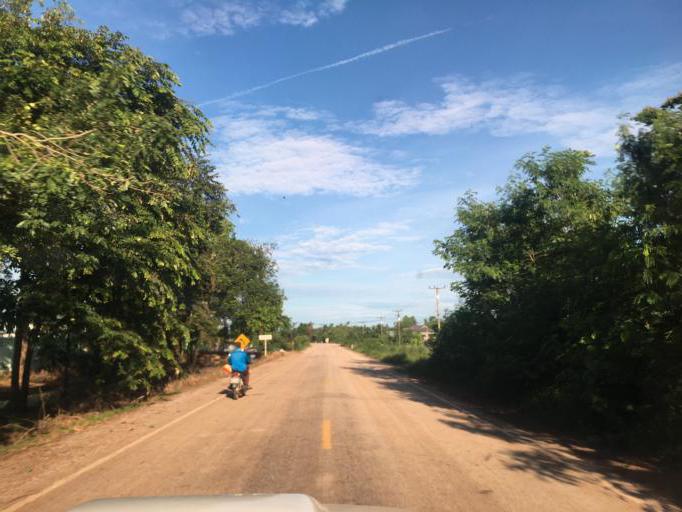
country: TH
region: Changwat Udon Thani
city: Kut Chap
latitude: 17.3831
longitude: 102.6119
